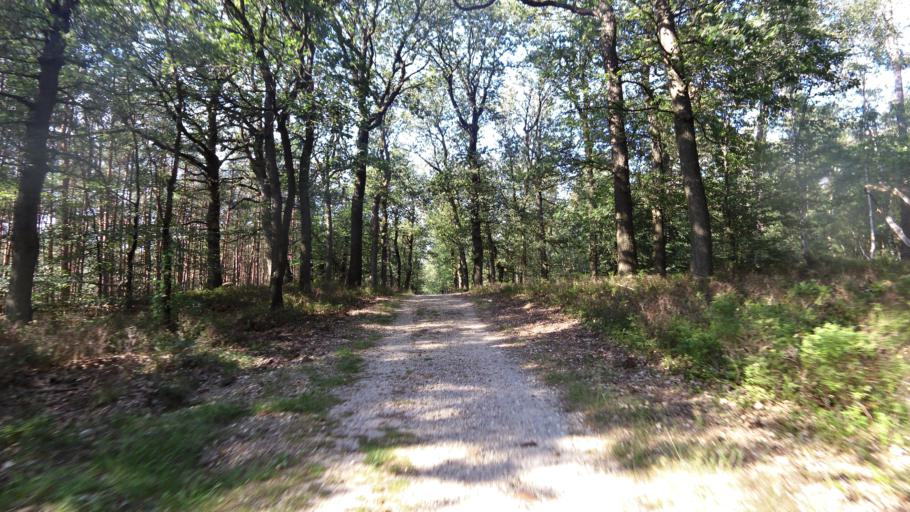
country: NL
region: Gelderland
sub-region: Gemeente Apeldoorn
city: Beekbergen
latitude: 52.1149
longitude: 5.9413
